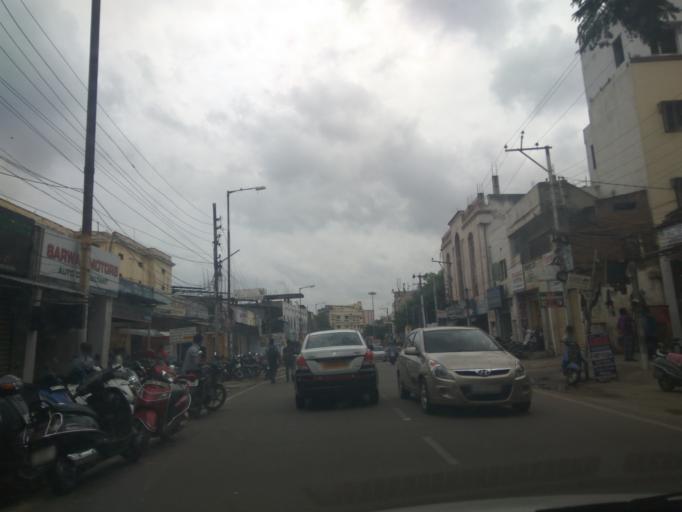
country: IN
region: Telangana
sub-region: Hyderabad
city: Hyderabad
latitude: 17.3945
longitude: 78.4851
